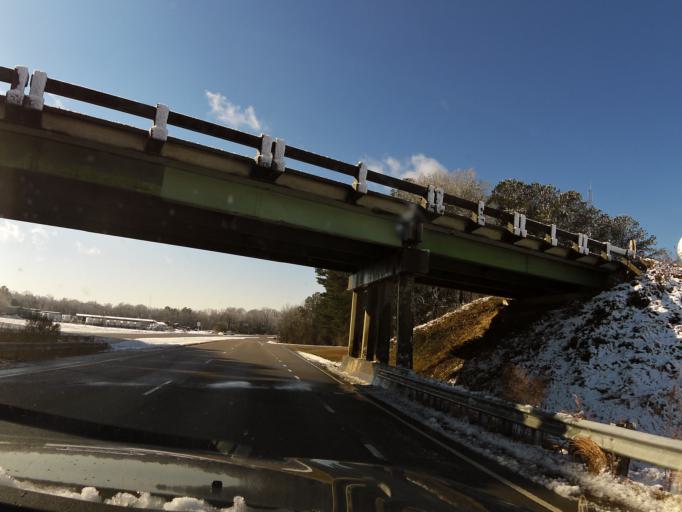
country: US
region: North Carolina
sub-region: Wilson County
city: Wilson
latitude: 35.7356
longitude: -77.8790
